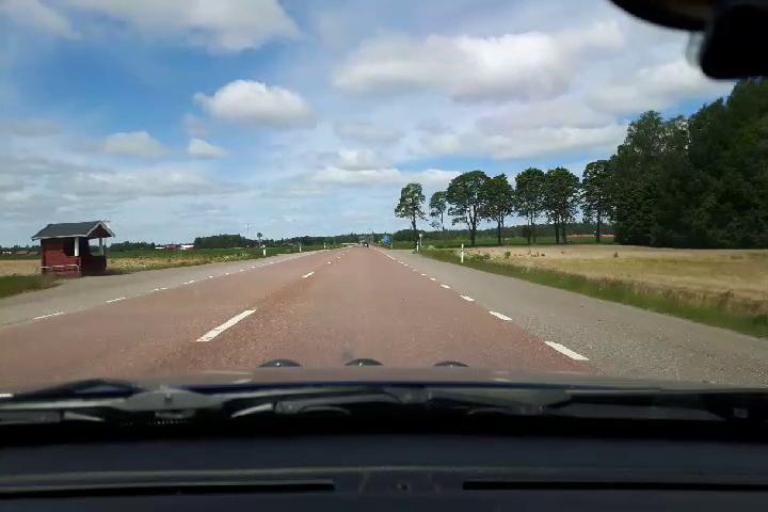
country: SE
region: Uppsala
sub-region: Osthammars Kommun
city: Bjorklinge
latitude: 60.0122
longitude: 17.5593
